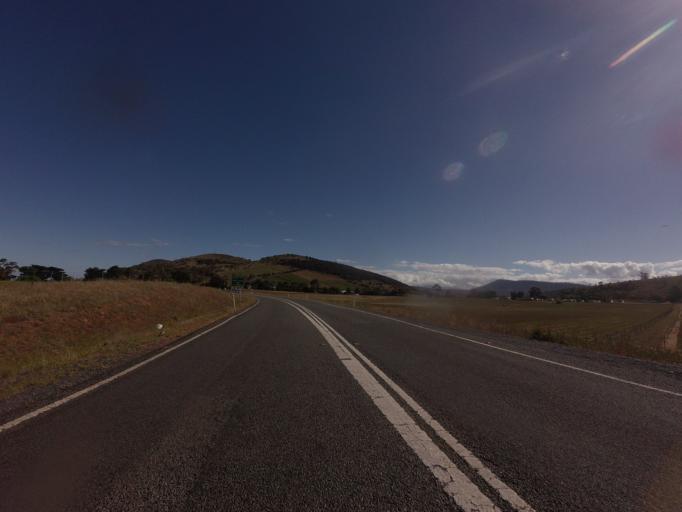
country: AU
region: Tasmania
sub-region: Clarence
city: Cambridge
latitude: -42.7355
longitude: 147.4303
